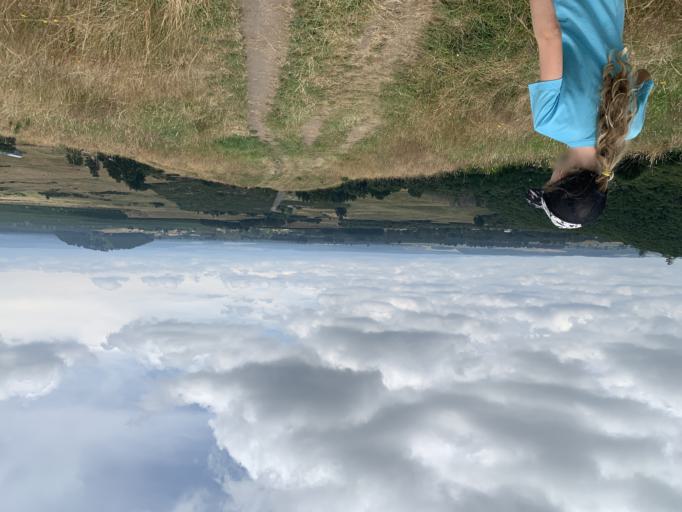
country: NZ
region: Waikato
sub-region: Taupo District
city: Taupo
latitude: -38.7005
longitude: 176.1422
